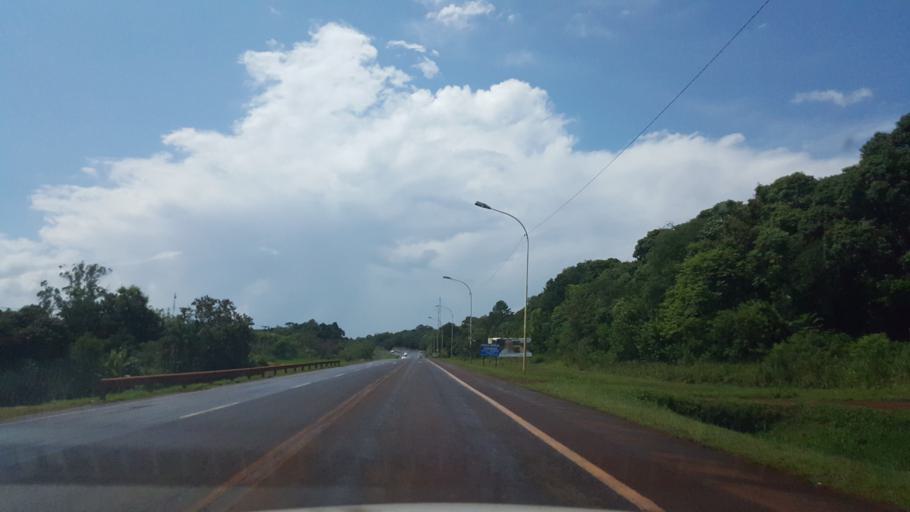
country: AR
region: Misiones
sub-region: Departamento de Eldorado
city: Eldorado
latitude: -26.4100
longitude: -54.6384
